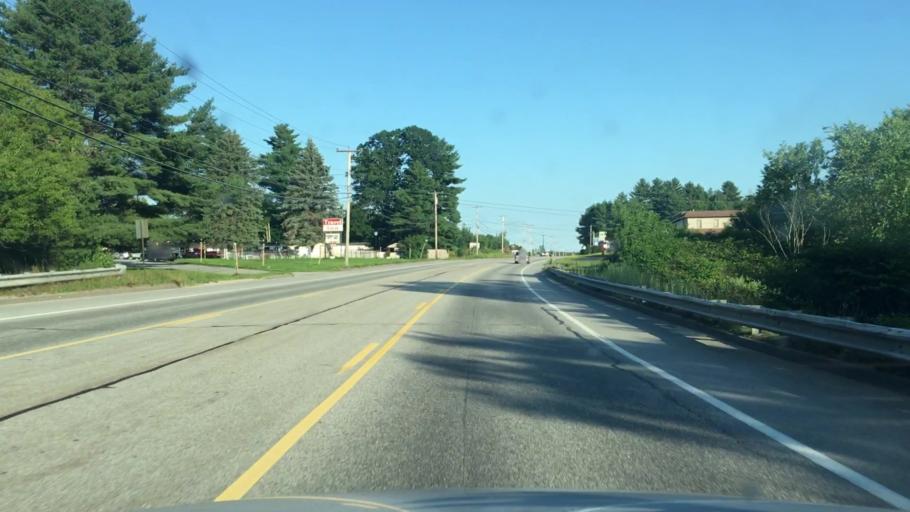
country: US
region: Maine
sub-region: Androscoggin County
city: Lisbon
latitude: 44.0611
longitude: -70.1476
